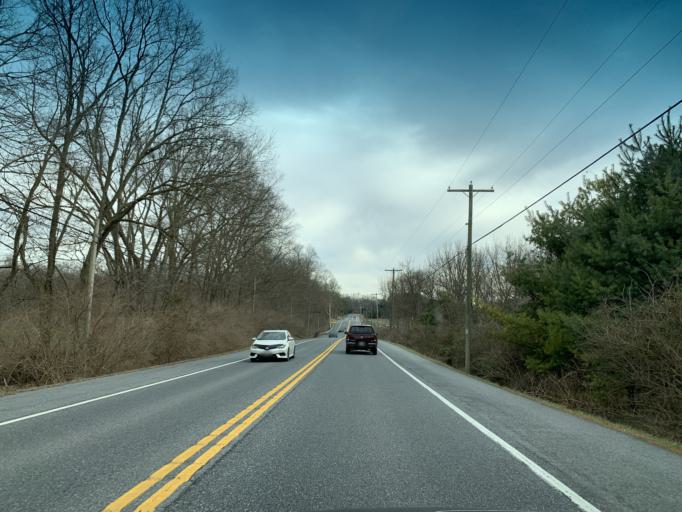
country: US
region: Maryland
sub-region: Washington County
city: Robinwood
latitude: 39.5860
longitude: -77.6965
